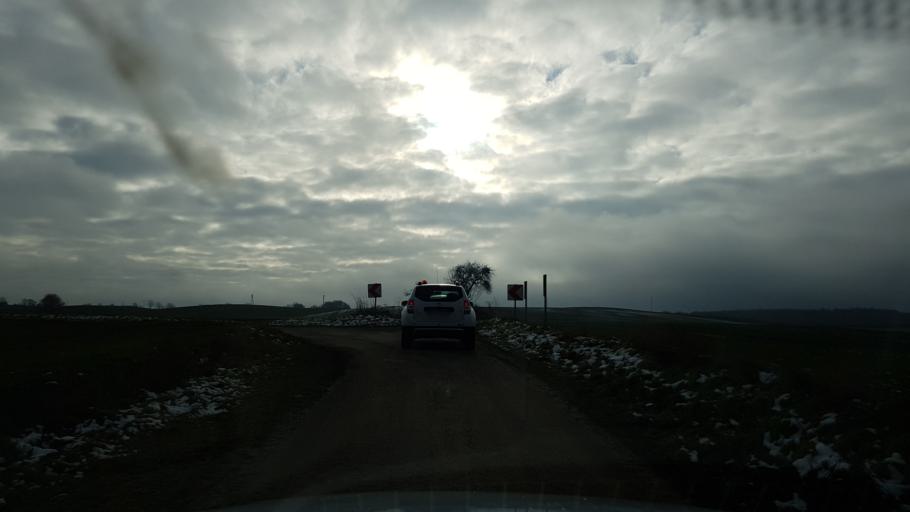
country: PL
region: West Pomeranian Voivodeship
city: Trzcinsko Zdroj
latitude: 52.9407
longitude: 14.7178
